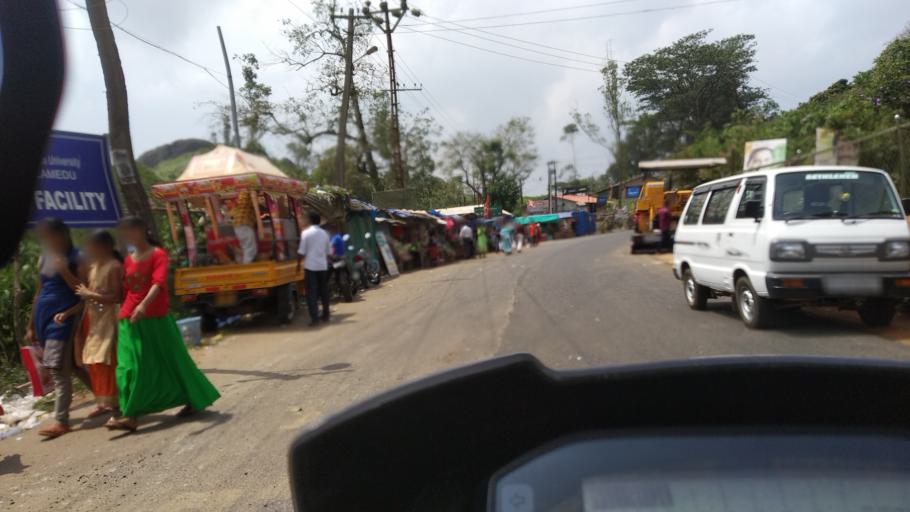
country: IN
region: Kerala
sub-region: Kottayam
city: Erattupetta
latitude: 9.6539
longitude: 76.9271
